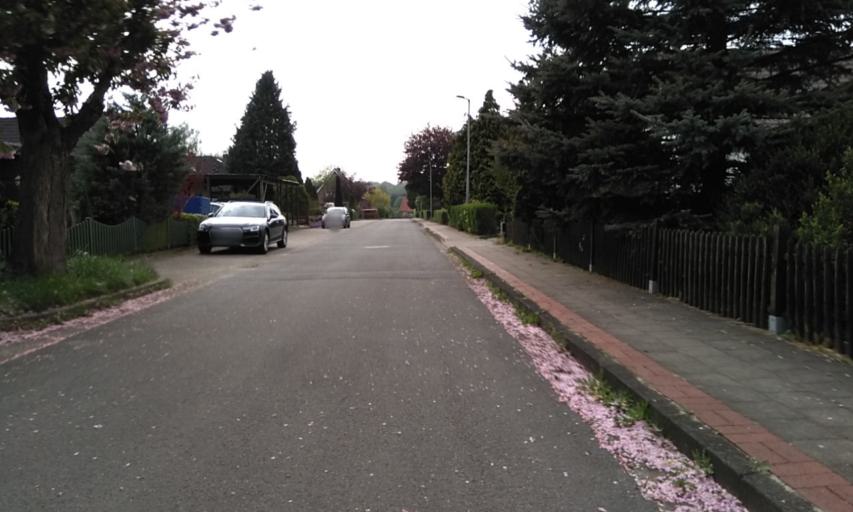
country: DE
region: Lower Saxony
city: Bliedersdorf
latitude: 53.4514
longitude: 9.5658
